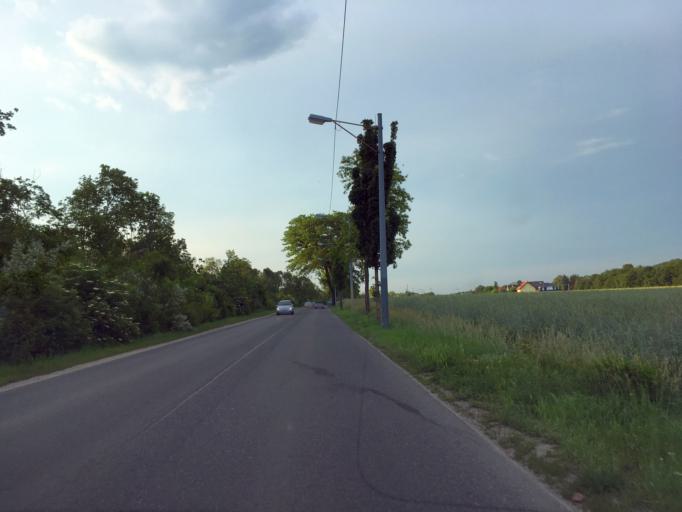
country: AT
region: Lower Austria
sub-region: Politischer Bezirk Wien-Umgebung
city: Gerasdorf bei Wien
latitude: 48.2711
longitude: 16.4568
